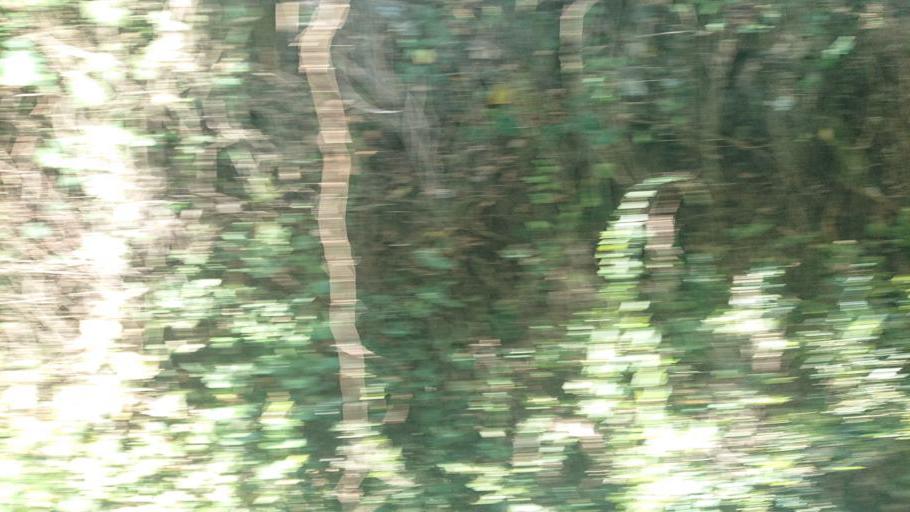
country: TW
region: Taiwan
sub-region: Chiayi
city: Jiayi Shi
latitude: 23.5356
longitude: 120.6359
